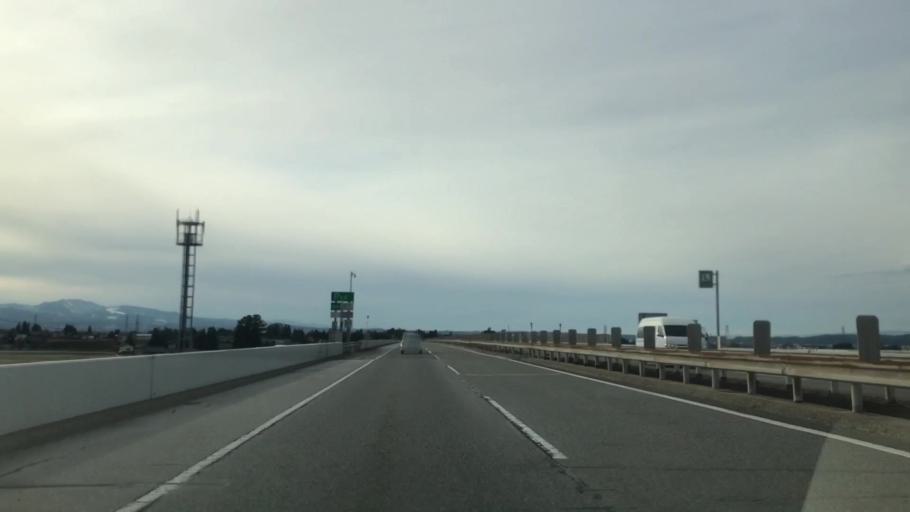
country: JP
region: Toyama
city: Toyama-shi
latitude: 36.6670
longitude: 137.2801
